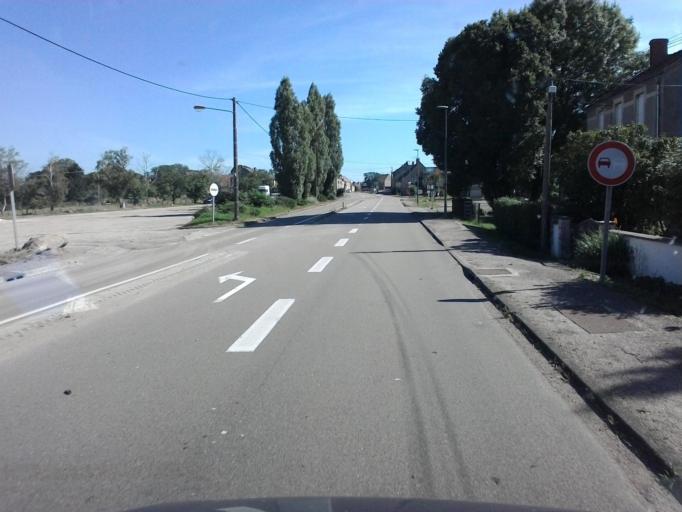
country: FR
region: Bourgogne
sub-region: Departement de la Cote-d'Or
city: Saulieu
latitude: 47.3838
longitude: 4.1747
